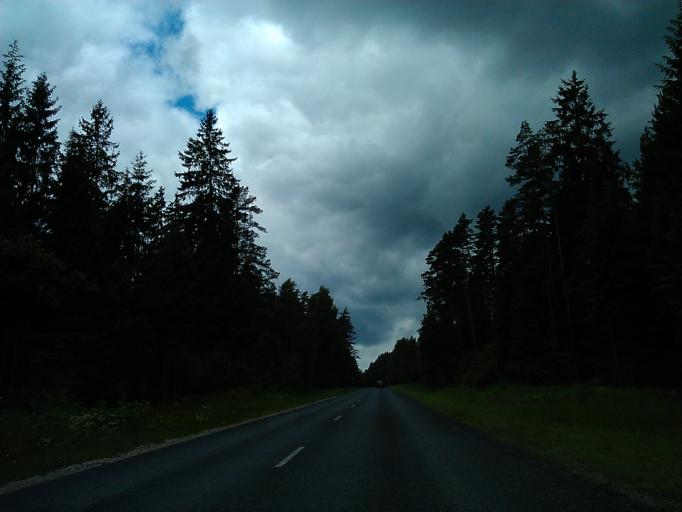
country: LV
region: Talsu Rajons
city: Stende
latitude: 57.0906
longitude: 22.3948
